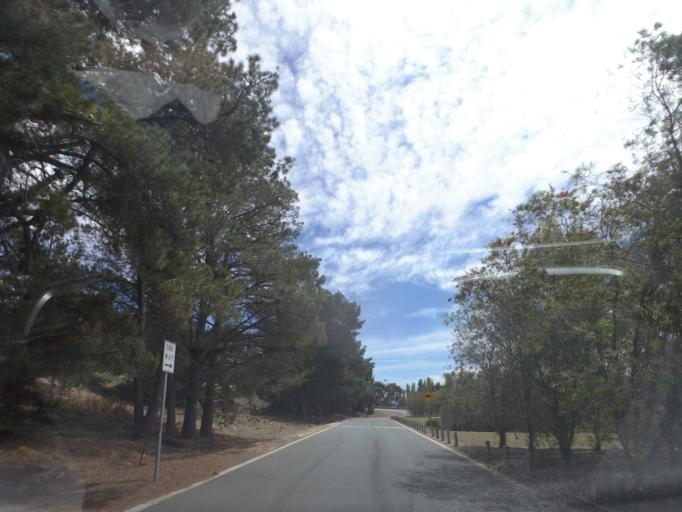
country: AU
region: New South Wales
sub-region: Yass Valley
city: Gundaroo
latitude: -35.1012
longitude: 149.3764
